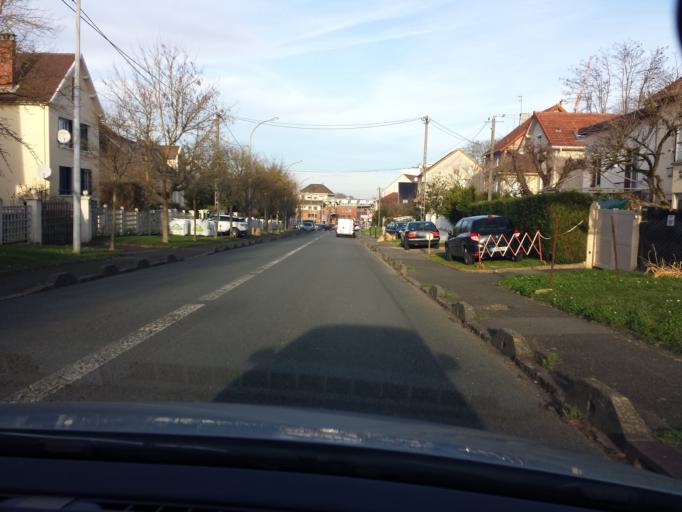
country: FR
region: Ile-de-France
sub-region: Departement de l'Essonne
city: Palaiseau
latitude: 48.7219
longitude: 2.2579
